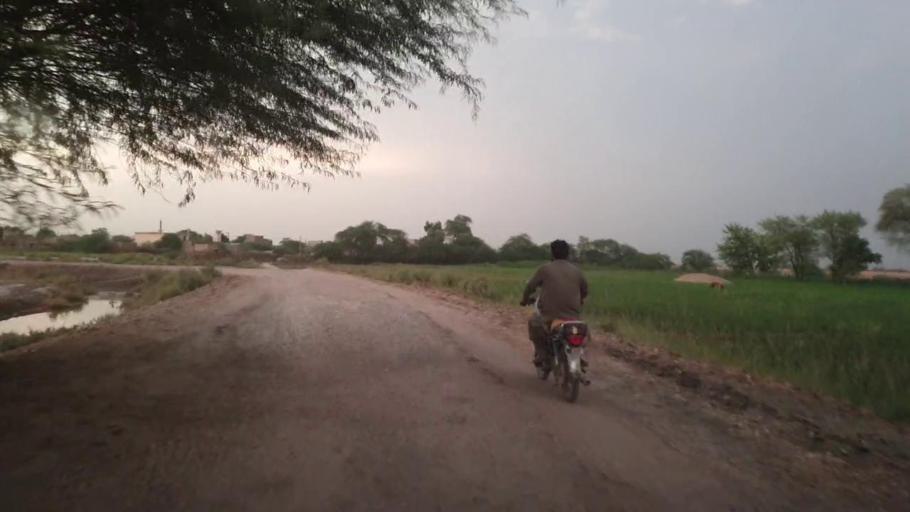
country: PK
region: Sindh
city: Karaundi
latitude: 27.0433
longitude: 68.3799
